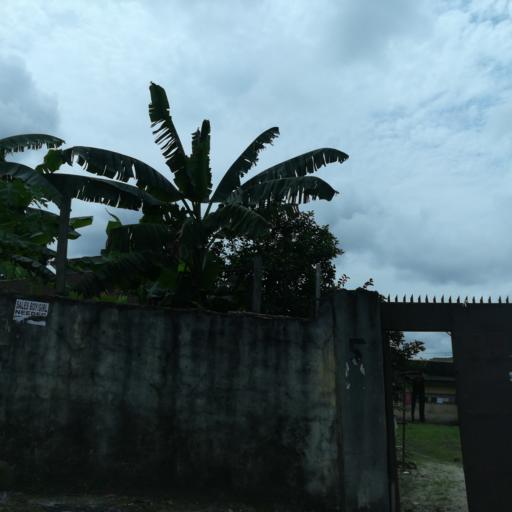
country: NG
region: Rivers
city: Port Harcourt
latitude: 4.7947
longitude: 7.0262
